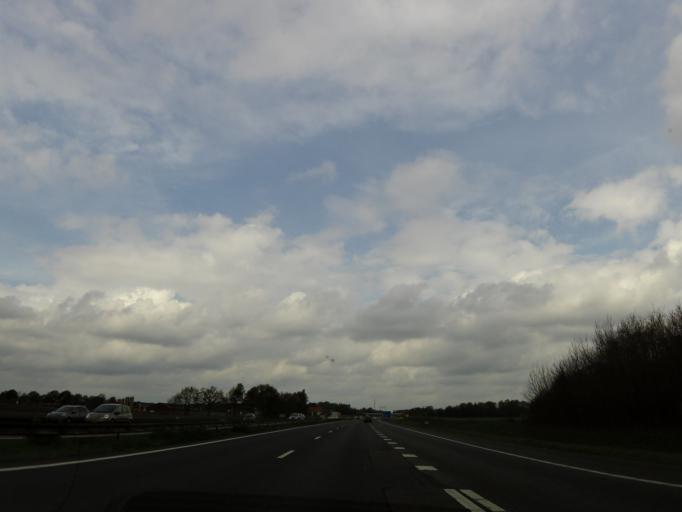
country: NL
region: Limburg
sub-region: Gemeente Leudal
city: Kelpen-Oler
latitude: 51.2378
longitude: 5.7911
